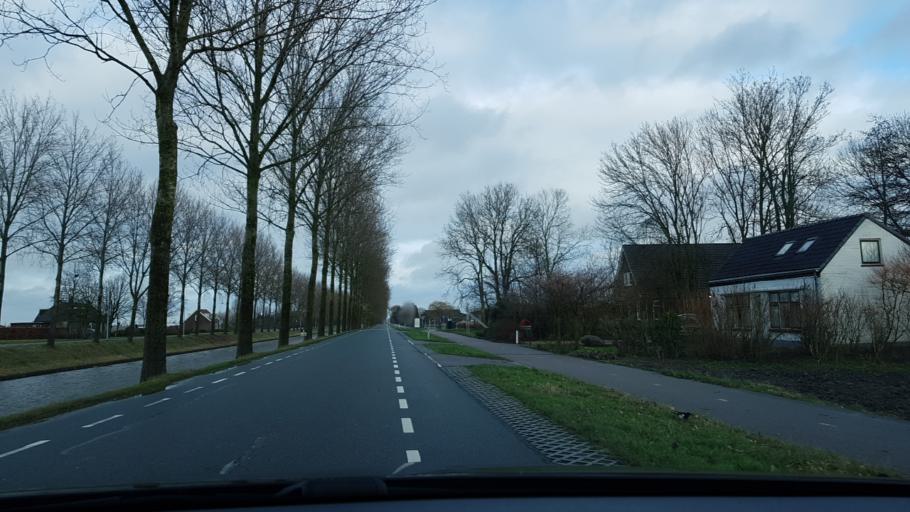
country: NL
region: North Holland
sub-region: Gemeente Haarlemmermeer
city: Hoofddorp
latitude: 52.2747
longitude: 4.6487
